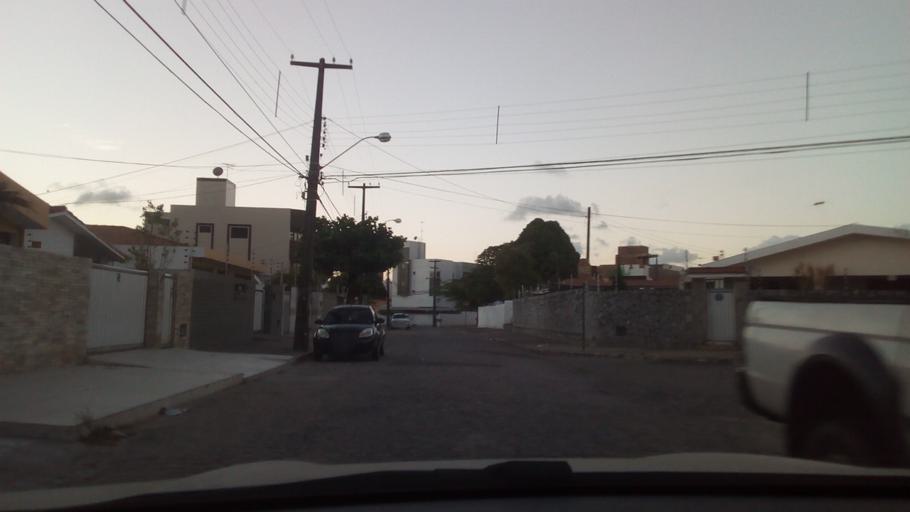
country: BR
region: Paraiba
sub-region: Joao Pessoa
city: Joao Pessoa
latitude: -7.1512
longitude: -34.8424
